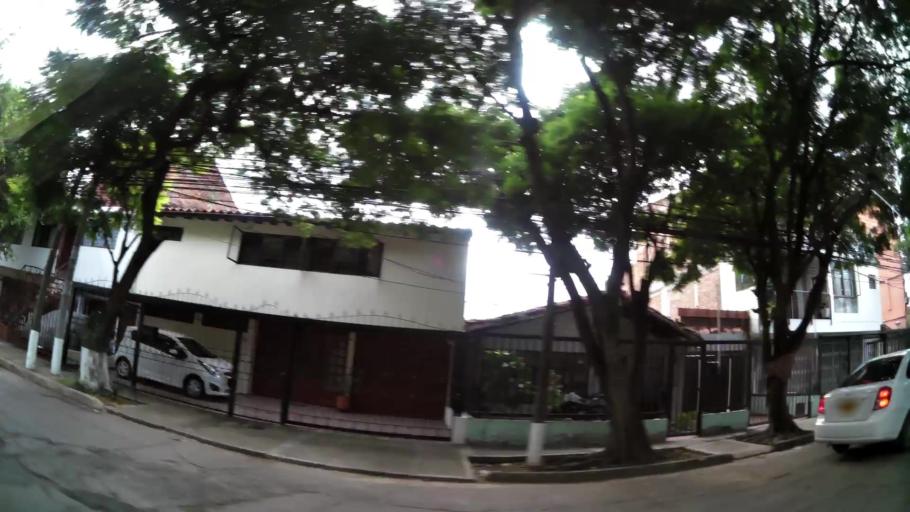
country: CO
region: Valle del Cauca
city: Cali
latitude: 3.4725
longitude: -76.5227
